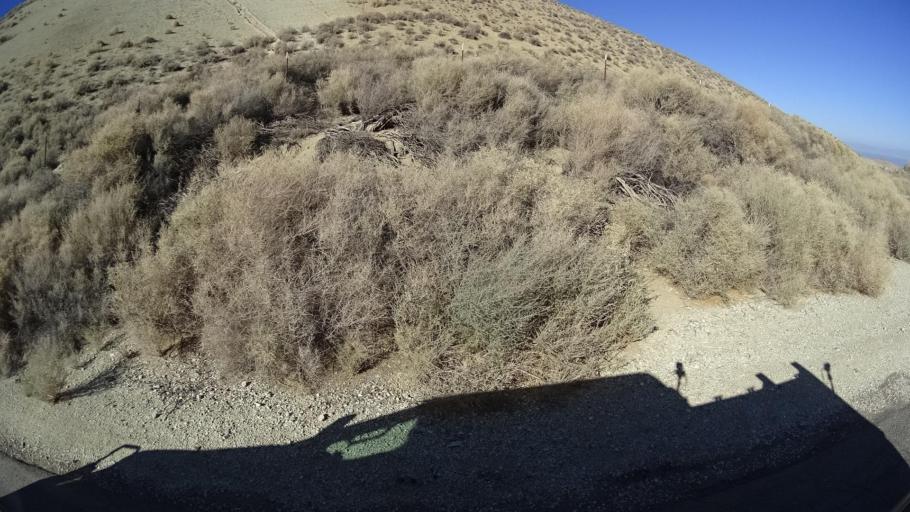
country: US
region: California
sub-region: Kern County
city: Maricopa
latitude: 34.9783
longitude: -119.4050
